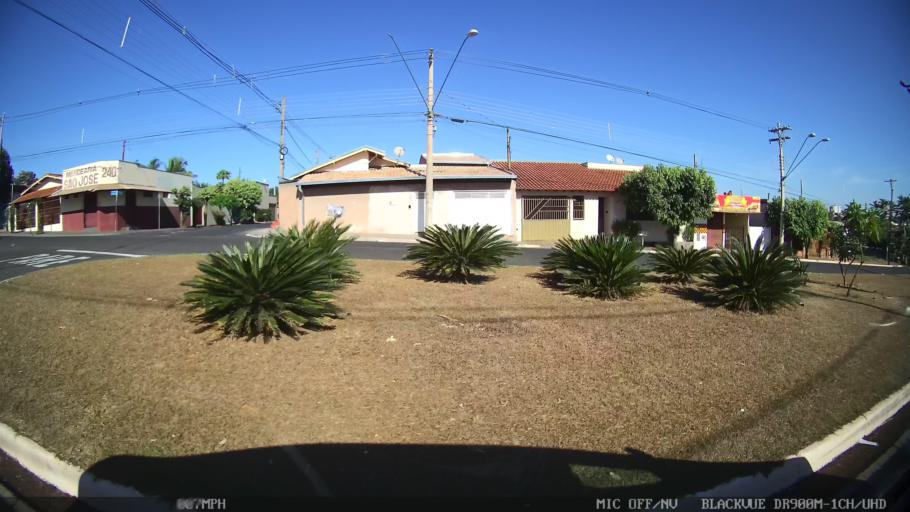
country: BR
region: Sao Paulo
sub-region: Olimpia
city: Olimpia
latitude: -20.7267
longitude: -48.9131
